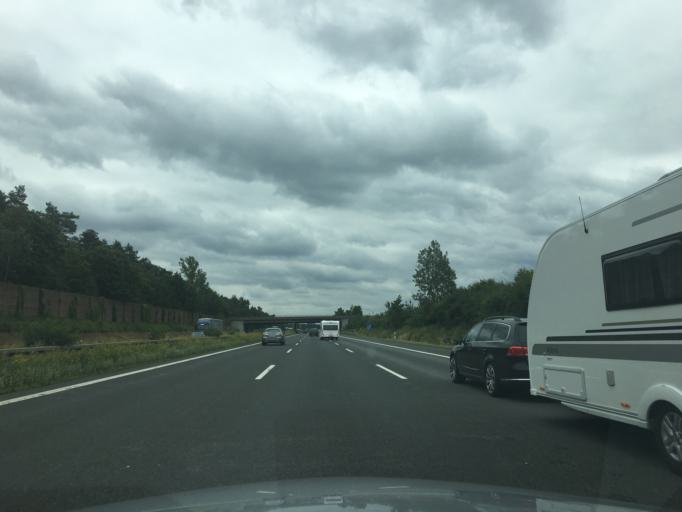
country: DE
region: Bavaria
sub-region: Regierungsbezirk Mittelfranken
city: Feucht
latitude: 49.3685
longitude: 11.2014
